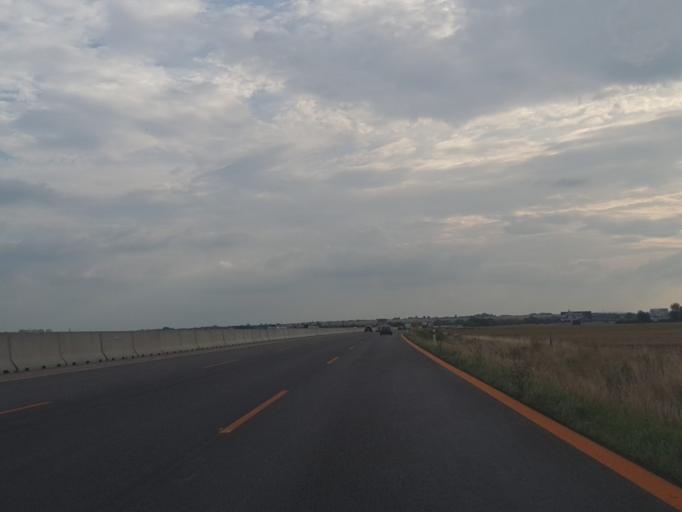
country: SK
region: Bratislavsky
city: Senec
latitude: 48.2526
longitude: 17.4346
